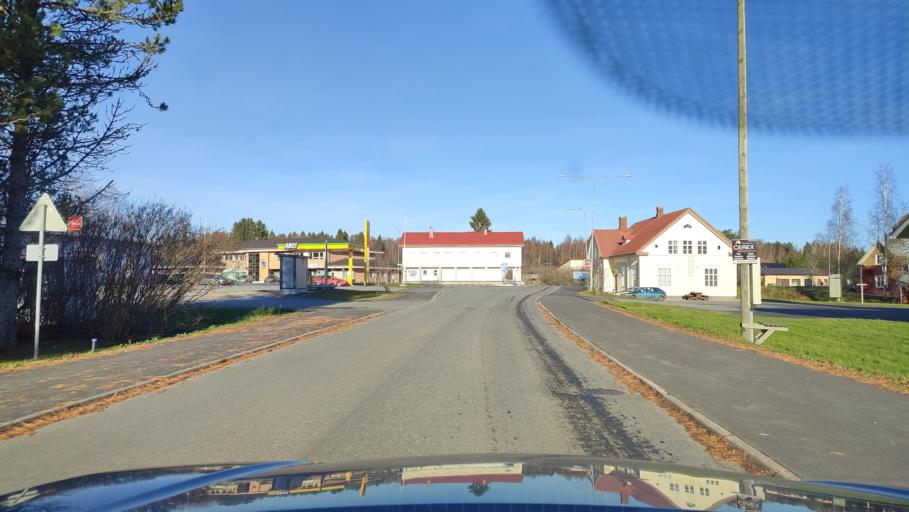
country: FI
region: Southern Ostrobothnia
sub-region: Suupohja
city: Karijoki
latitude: 62.3069
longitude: 21.7074
